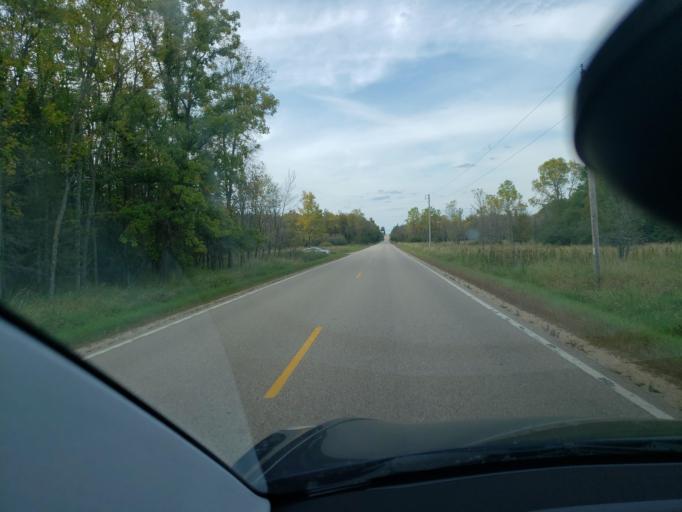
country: US
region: Wisconsin
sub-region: Waupaca County
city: Marion
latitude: 44.7551
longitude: -88.8989
